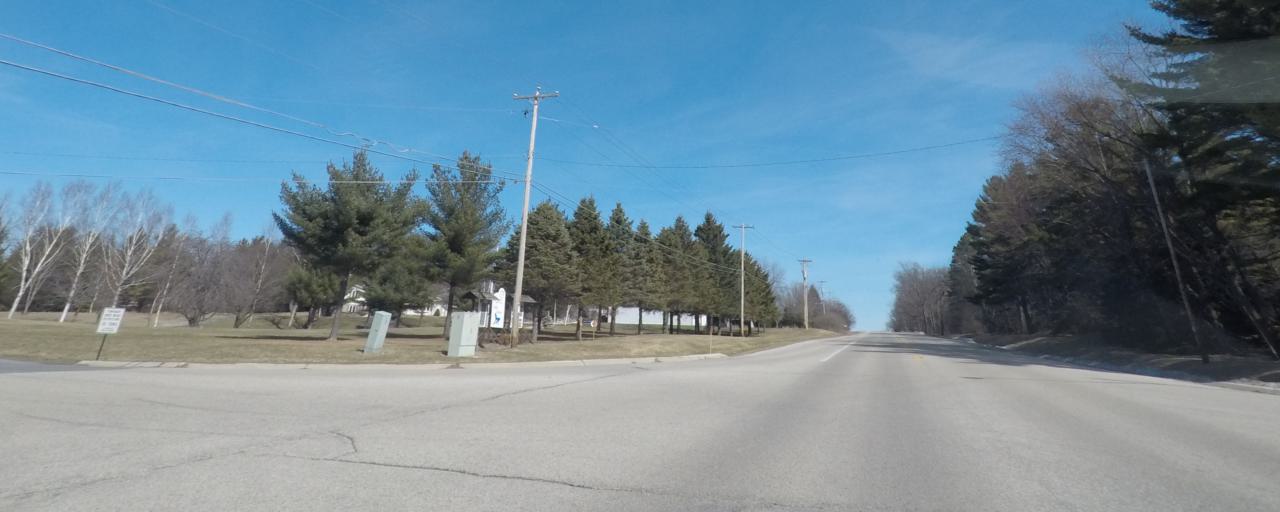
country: US
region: Wisconsin
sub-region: Waukesha County
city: Merton
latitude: 43.1558
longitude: -88.3217
